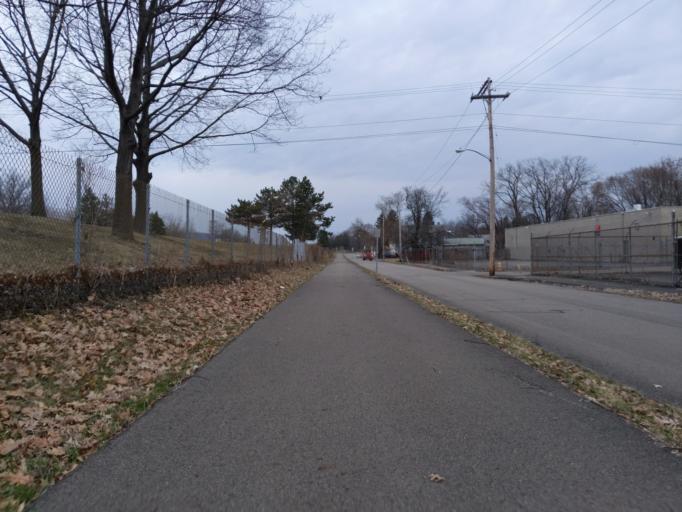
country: US
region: New York
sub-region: Chemung County
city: Elmira
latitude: 42.1075
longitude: -76.8117
